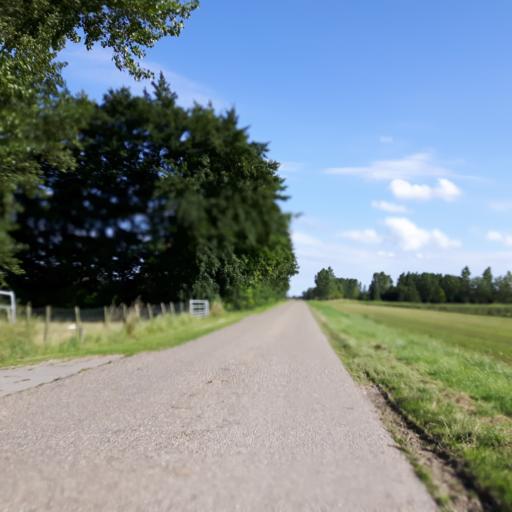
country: NL
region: Zeeland
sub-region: Gemeente Goes
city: Goes
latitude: 51.5287
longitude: 3.9173
